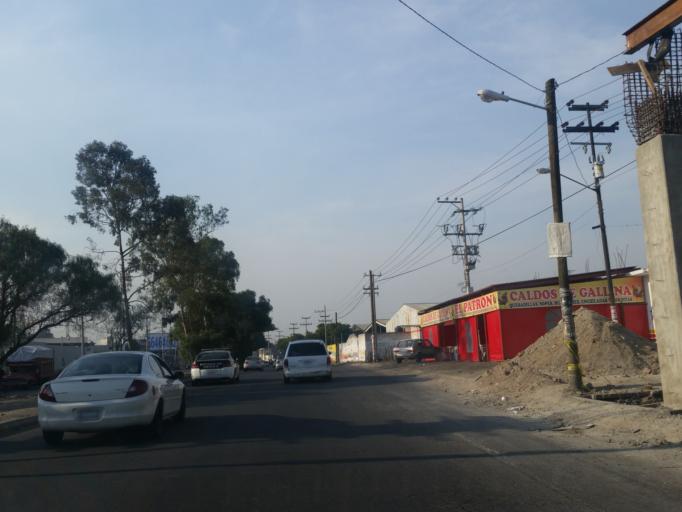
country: MX
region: Mexico
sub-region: La Paz
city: San Isidro
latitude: 19.3363
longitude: -98.9540
